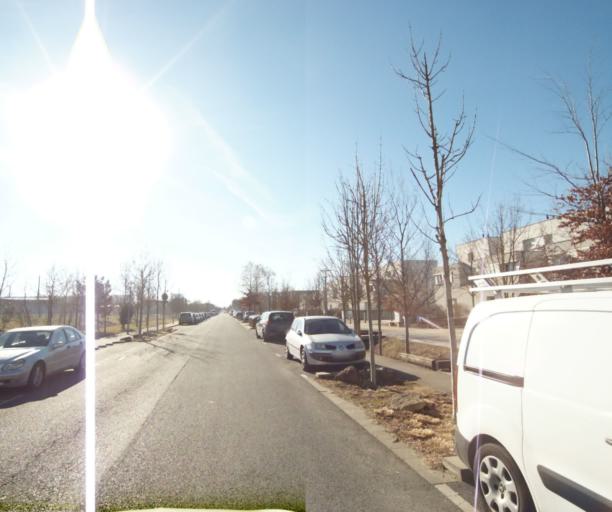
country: FR
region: Lorraine
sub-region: Departement de Meurthe-et-Moselle
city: Maxeville
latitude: 48.7078
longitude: 6.1479
